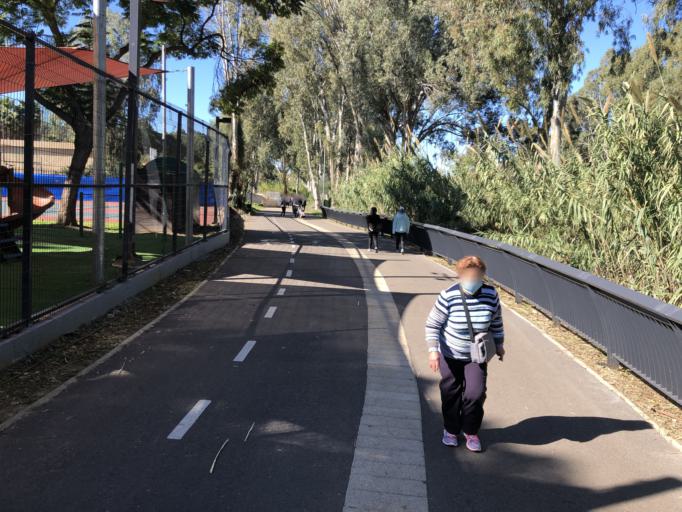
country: IL
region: Tel Aviv
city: Ramat Gan
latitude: 32.0961
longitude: 34.8103
